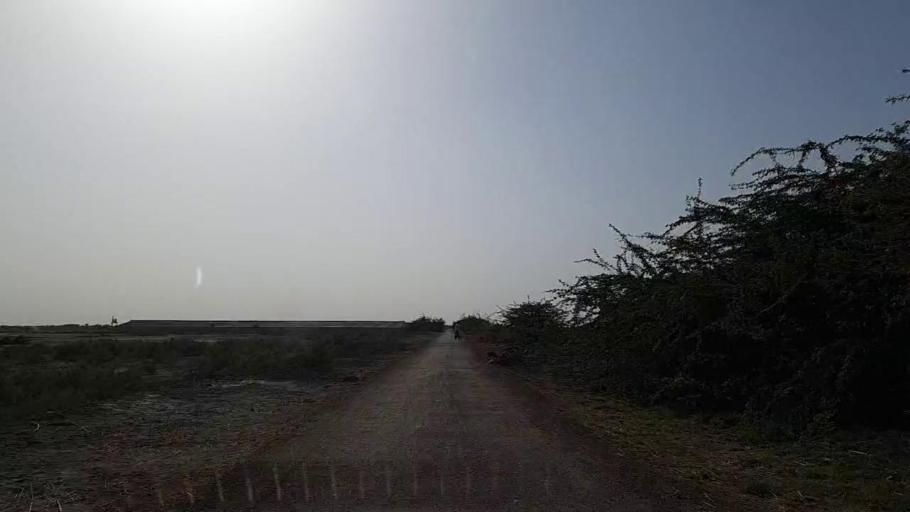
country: PK
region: Sindh
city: Jati
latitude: 24.2820
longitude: 68.2350
